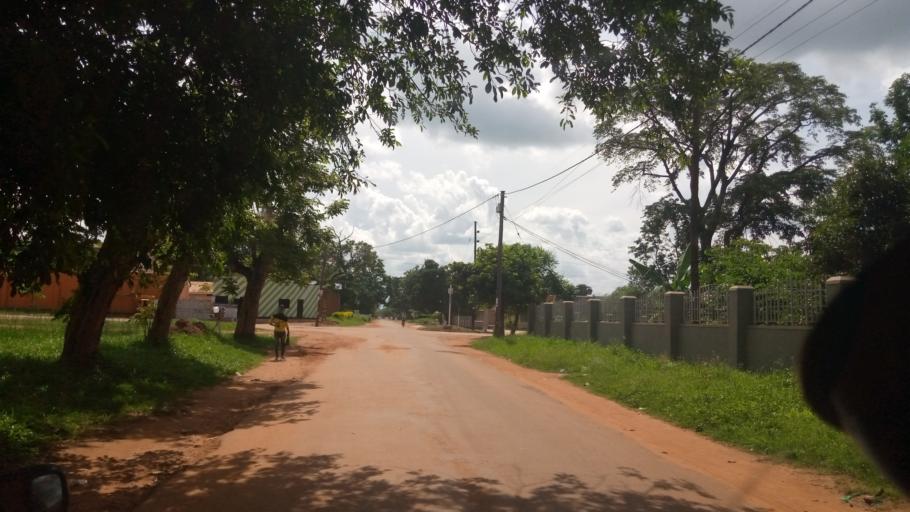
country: UG
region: Northern Region
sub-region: Lira District
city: Lira
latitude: 2.2513
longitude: 32.9008
